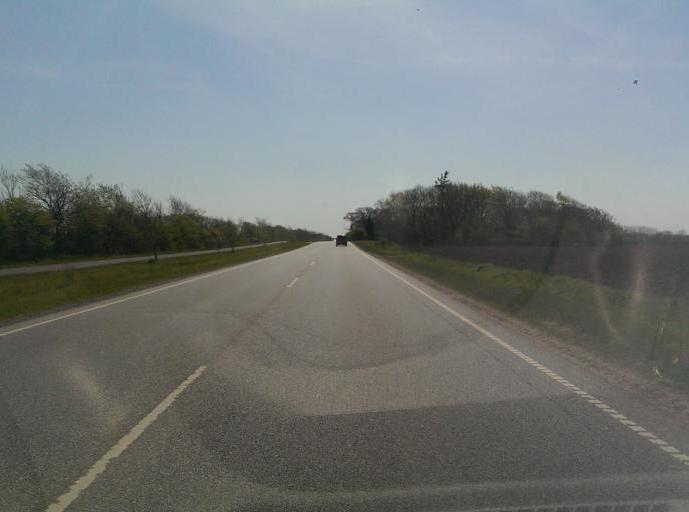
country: DK
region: South Denmark
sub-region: Esbjerg Kommune
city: Ribe
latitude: 55.3727
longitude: 8.7631
